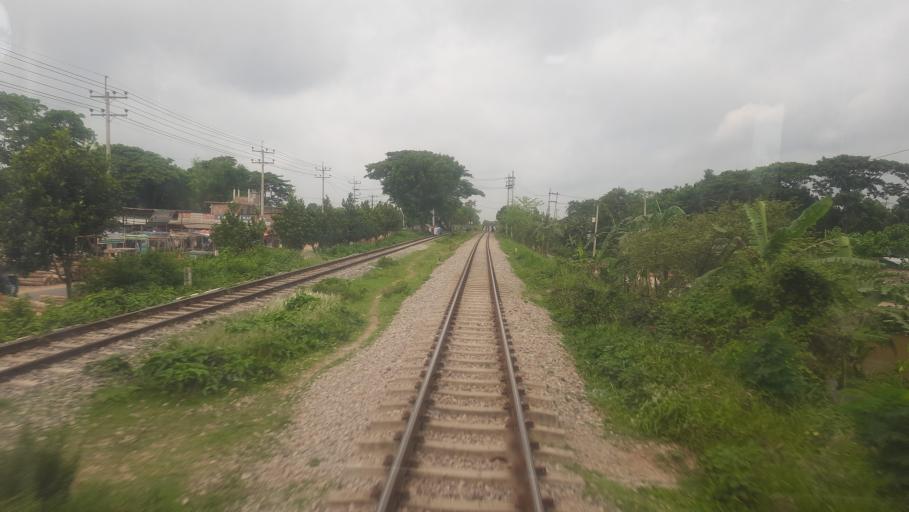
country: BD
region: Dhaka
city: Narsingdi
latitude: 23.9318
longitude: 90.7424
